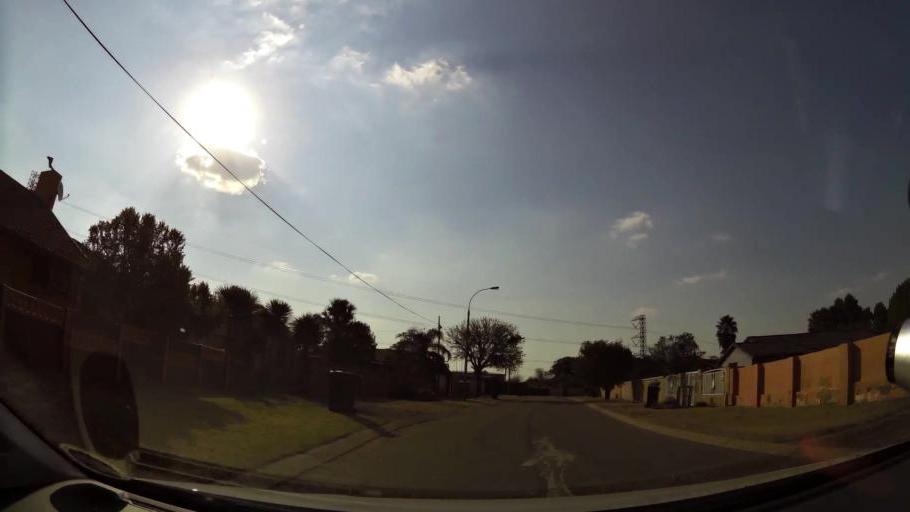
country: ZA
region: Gauteng
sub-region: City of Johannesburg Metropolitan Municipality
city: Modderfontein
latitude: -26.0805
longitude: 28.1905
